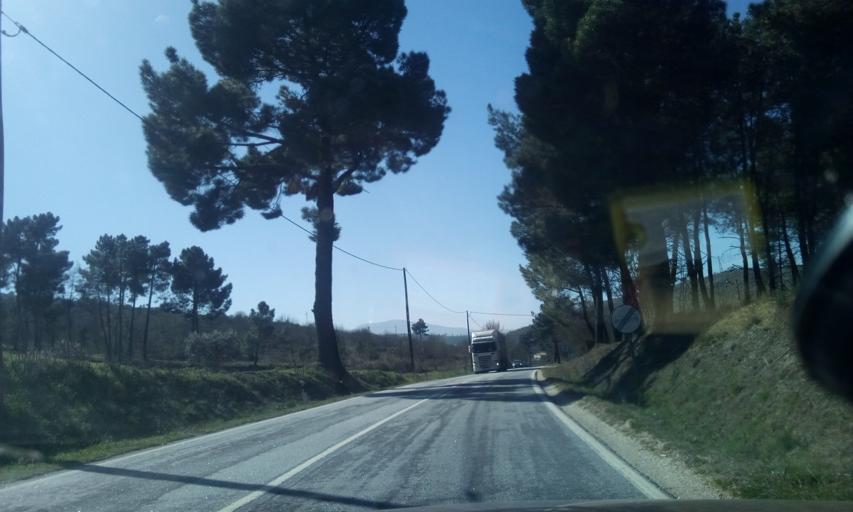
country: PT
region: Guarda
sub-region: Celorico da Beira
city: Celorico da Beira
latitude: 40.6073
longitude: -7.4182
